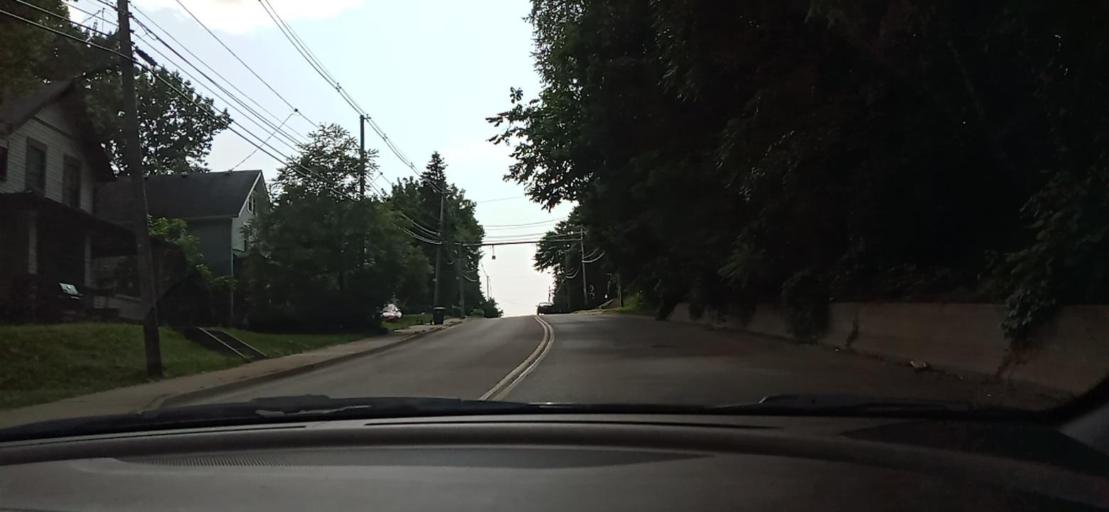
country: US
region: Ohio
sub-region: Summit County
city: Akron
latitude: 41.0700
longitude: -81.5508
